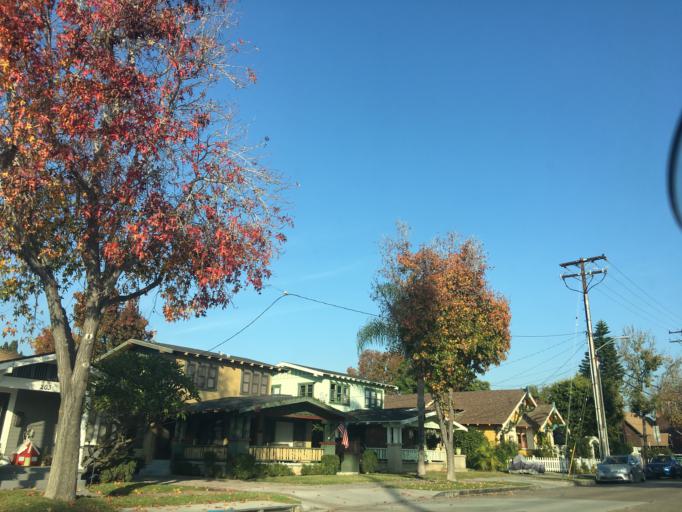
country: US
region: California
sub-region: Orange County
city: Orange
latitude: 33.7896
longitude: -117.8522
